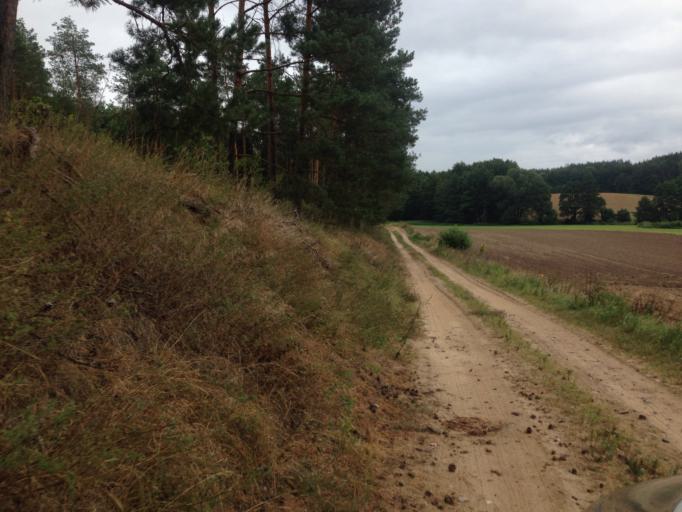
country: PL
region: Kujawsko-Pomorskie
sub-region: Powiat brodnicki
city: Bartniczka
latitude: 53.2752
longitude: 19.6296
